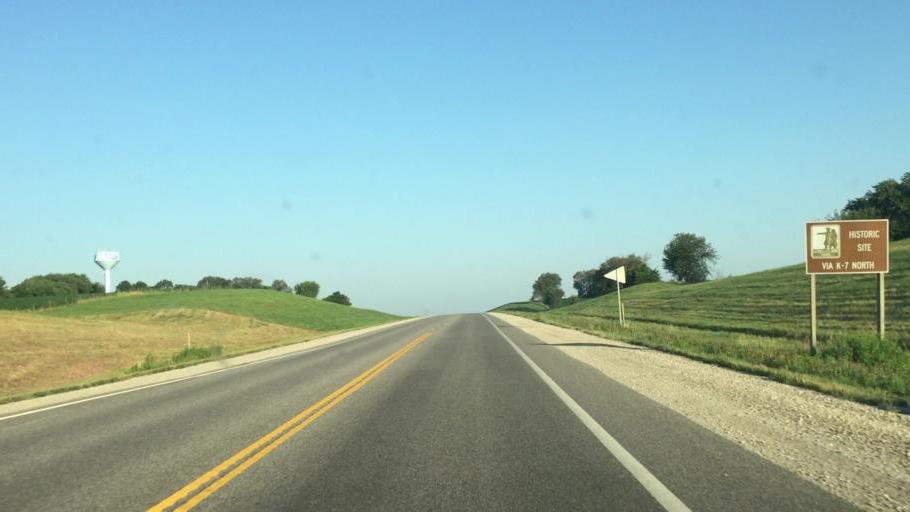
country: US
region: Kansas
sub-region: Doniphan County
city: Troy
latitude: 39.7931
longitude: -95.0768
